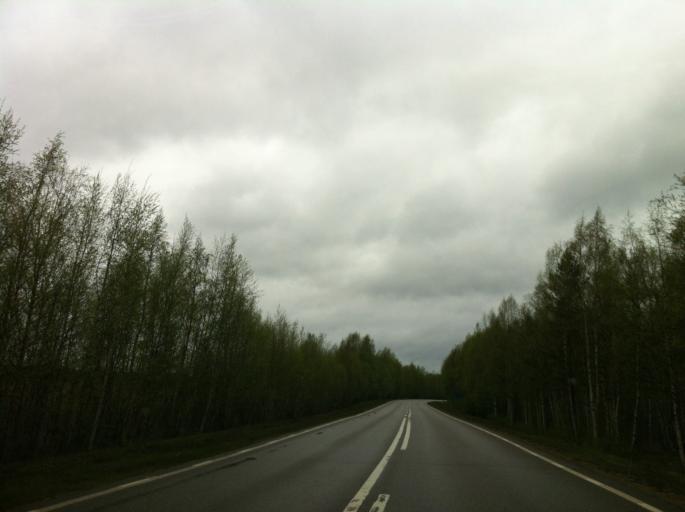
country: SE
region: Jaemtland
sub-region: Harjedalens Kommun
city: Sveg
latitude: 62.1280
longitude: 14.0656
